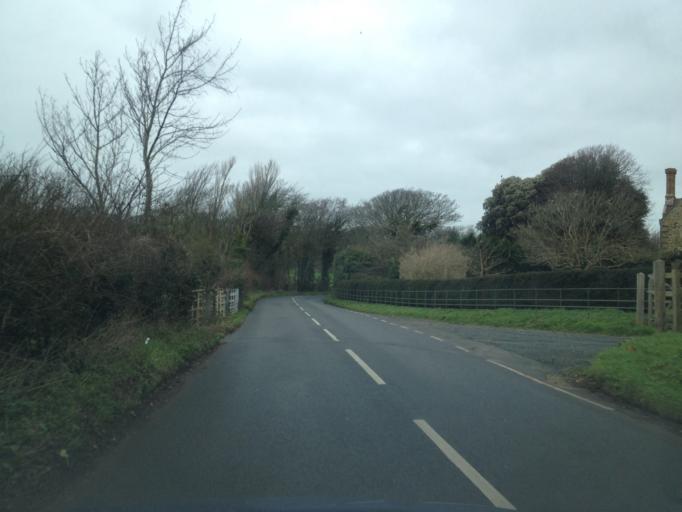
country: GB
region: England
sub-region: Isle of Wight
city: Brading
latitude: 50.6690
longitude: -1.1325
